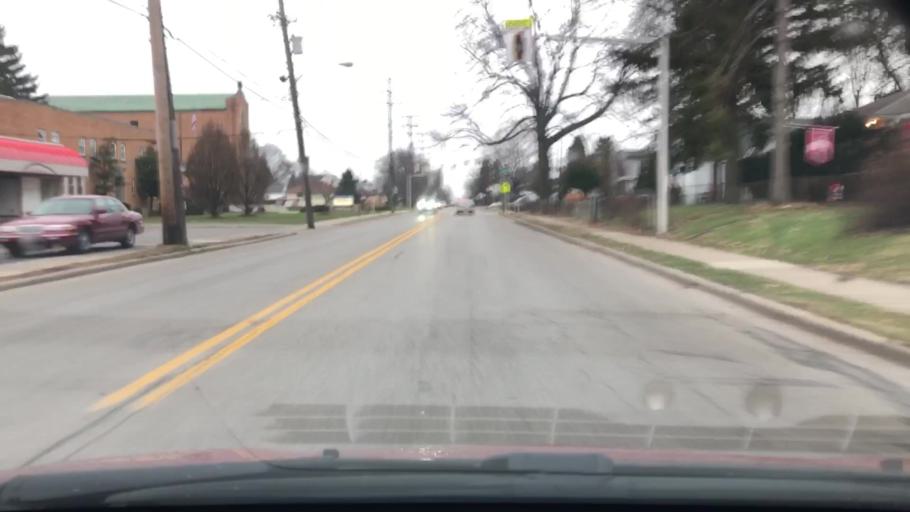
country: US
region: Ohio
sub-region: Franklin County
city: Minerva Park
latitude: 40.0316
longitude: -82.9707
